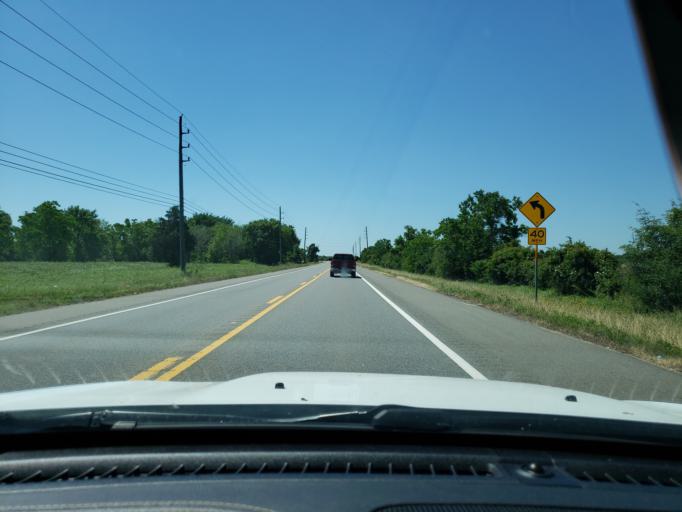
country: US
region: Texas
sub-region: Fort Bend County
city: Fulshear
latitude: 29.6893
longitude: -95.8460
